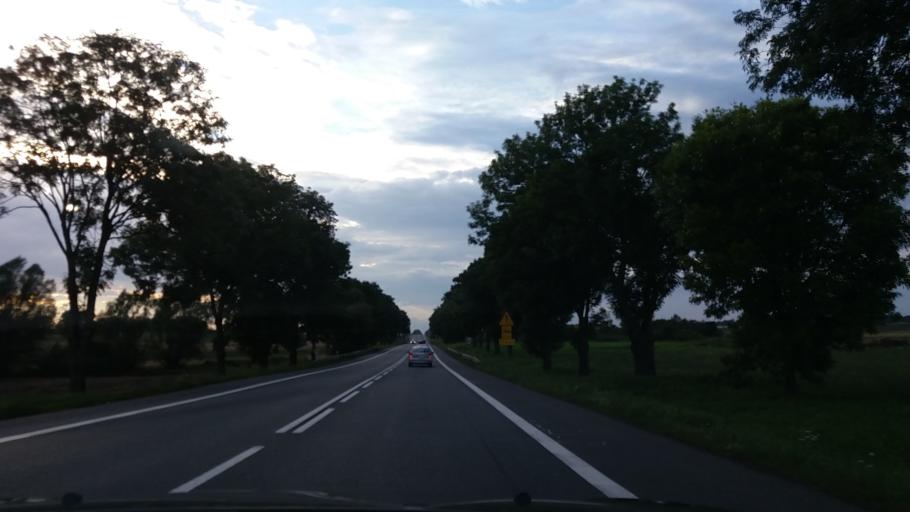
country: PL
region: Lower Silesian Voivodeship
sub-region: Powiat polkowicki
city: Gaworzyce
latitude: 51.6322
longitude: 15.9014
